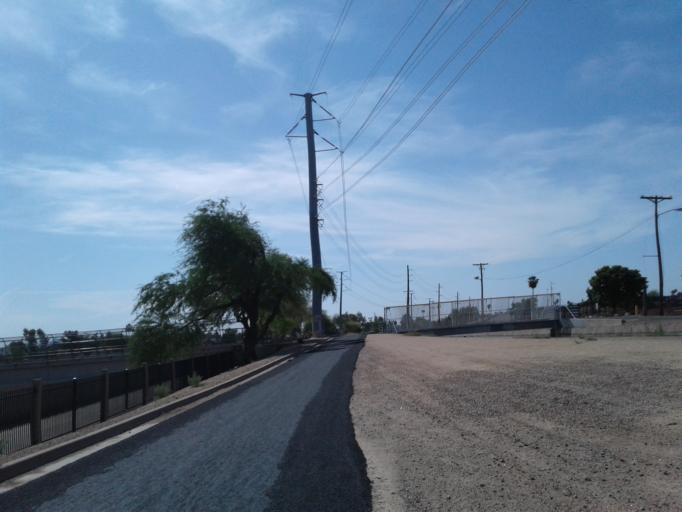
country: US
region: Arizona
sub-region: Maricopa County
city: Glendale
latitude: 33.5885
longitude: -112.1604
